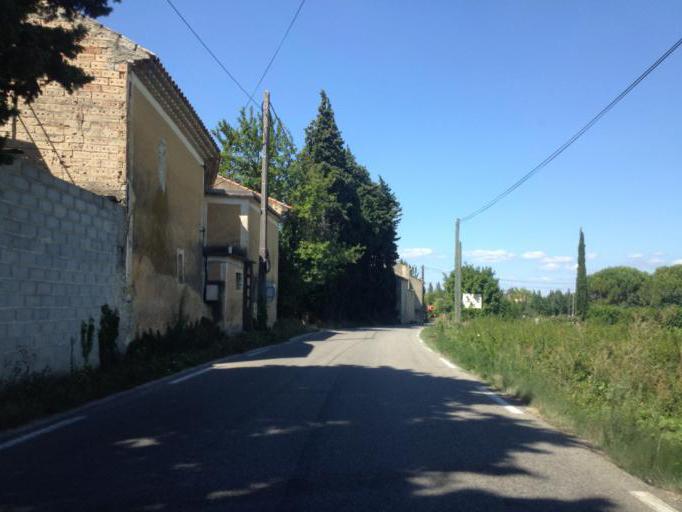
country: FR
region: Provence-Alpes-Cote d'Azur
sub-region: Departement du Vaucluse
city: Orange
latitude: 44.0961
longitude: 4.8068
